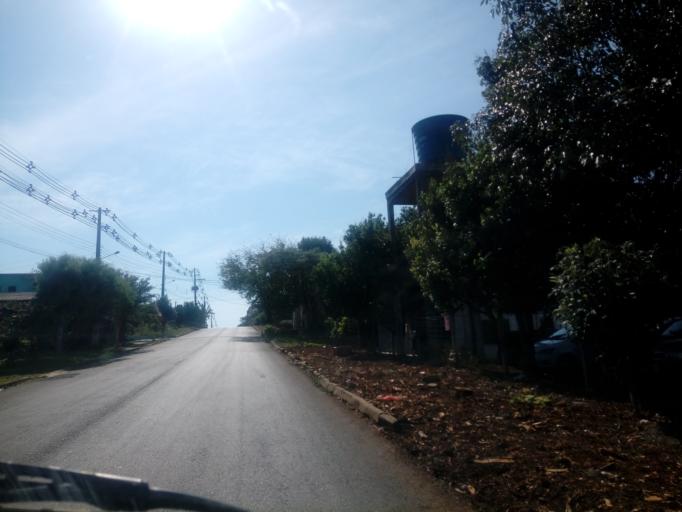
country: BR
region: Santa Catarina
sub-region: Chapeco
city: Chapeco
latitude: -27.0830
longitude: -52.6419
